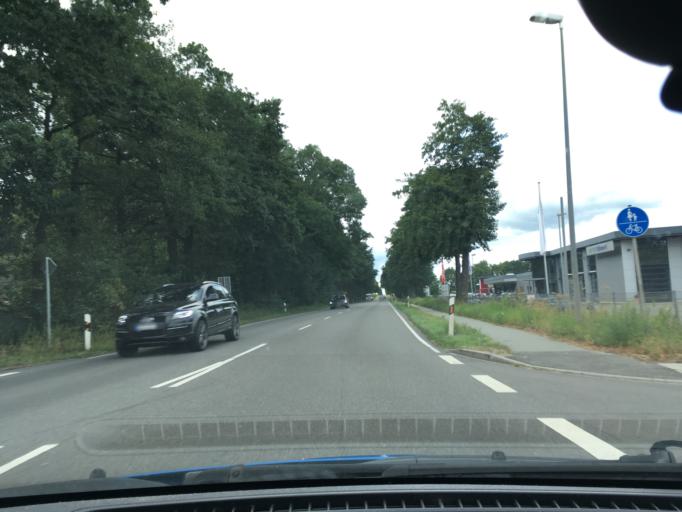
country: DE
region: Lower Saxony
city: Neu Wulmstorf
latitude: 53.4281
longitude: 9.7826
